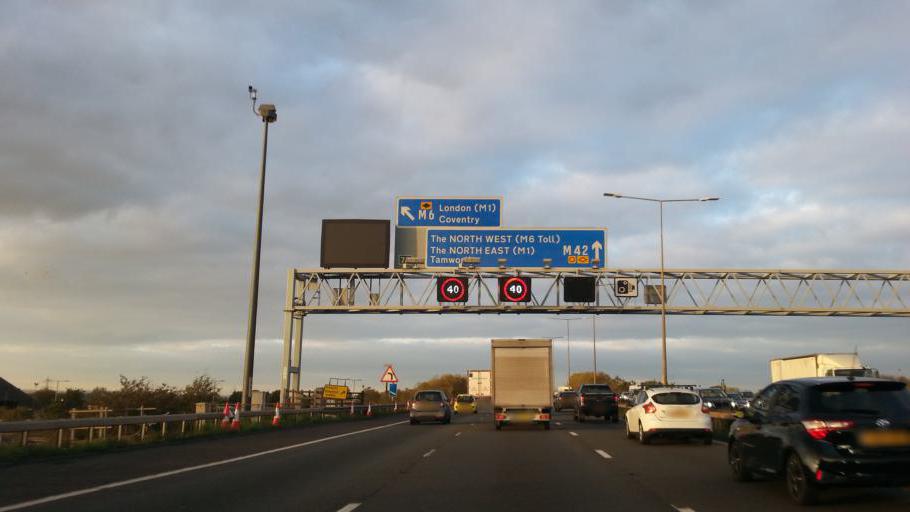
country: GB
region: England
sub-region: Solihull
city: Chelmsley Wood
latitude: 52.4763
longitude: -1.7111
